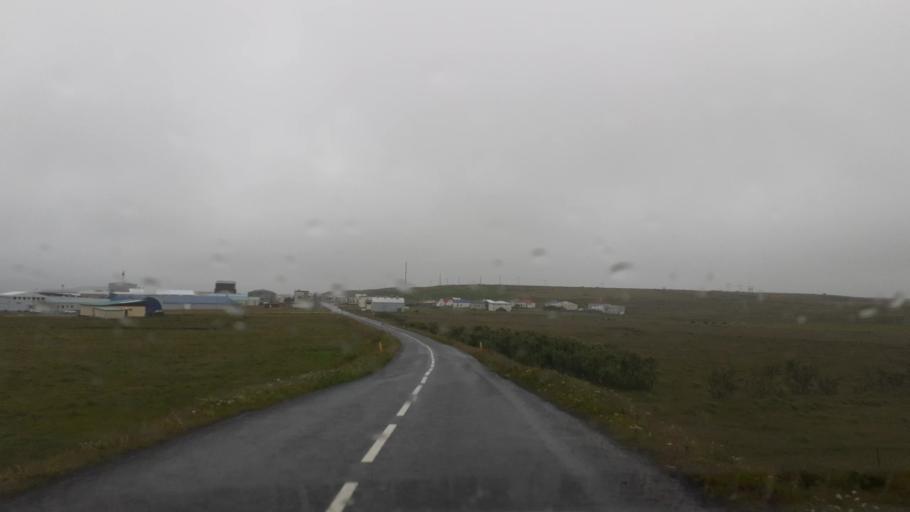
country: IS
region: Northeast
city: Husavik
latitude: 66.4601
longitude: -15.9518
